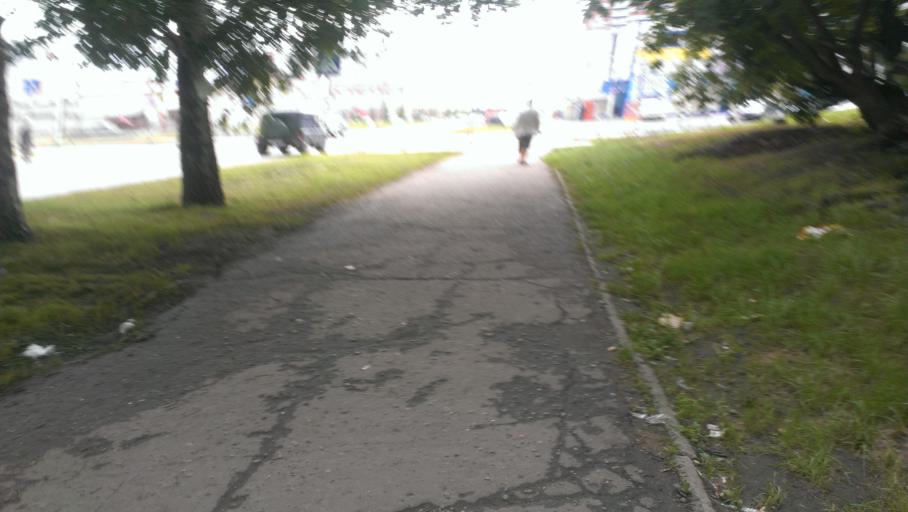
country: RU
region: Altai Krai
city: Novosilikatnyy
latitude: 53.3311
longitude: 83.6758
